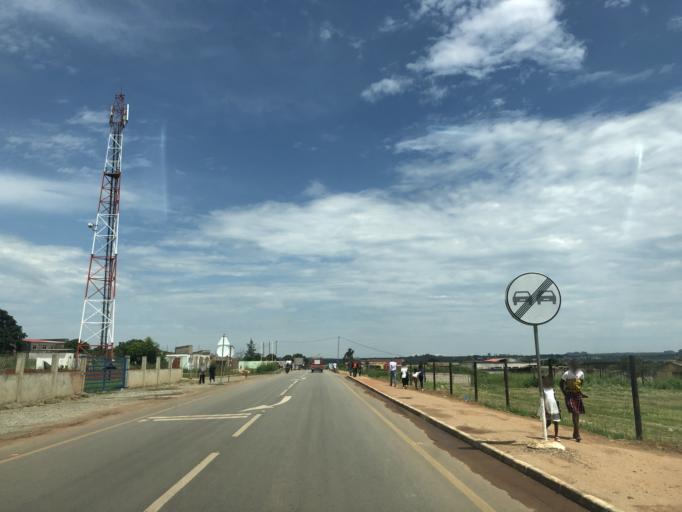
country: AO
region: Cuanza Sul
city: Quibala
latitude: -10.7346
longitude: 14.9816
